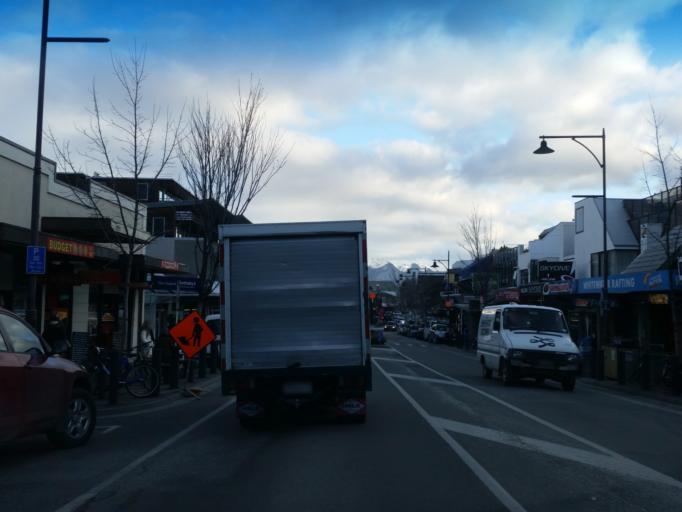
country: NZ
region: Otago
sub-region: Queenstown-Lakes District
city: Queenstown
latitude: -45.0311
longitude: 168.6602
